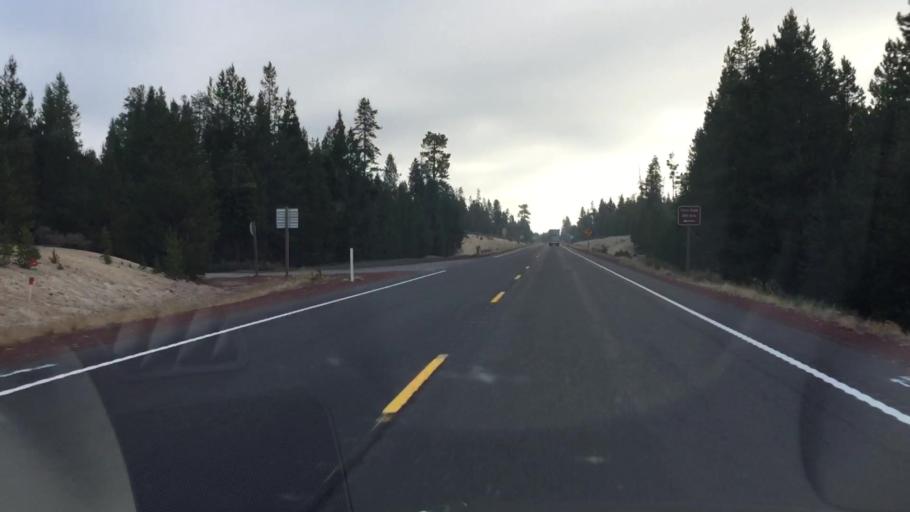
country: US
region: Oregon
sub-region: Deschutes County
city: La Pine
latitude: 43.3180
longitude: -121.7644
